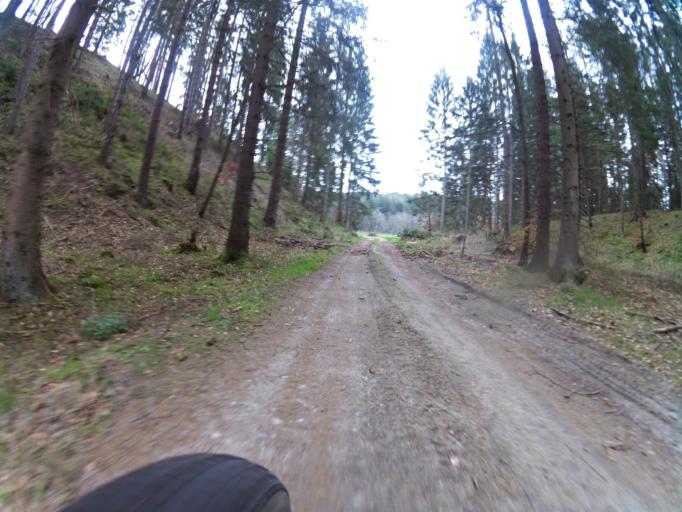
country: PL
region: West Pomeranian Voivodeship
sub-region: Powiat koszalinski
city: Polanow
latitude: 54.1913
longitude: 16.6853
